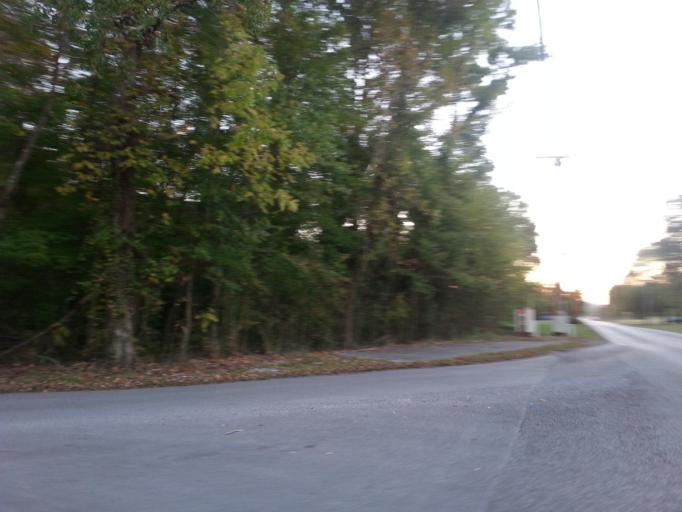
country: US
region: Tennessee
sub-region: Blount County
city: Wildwood
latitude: 35.7829
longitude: -83.8299
